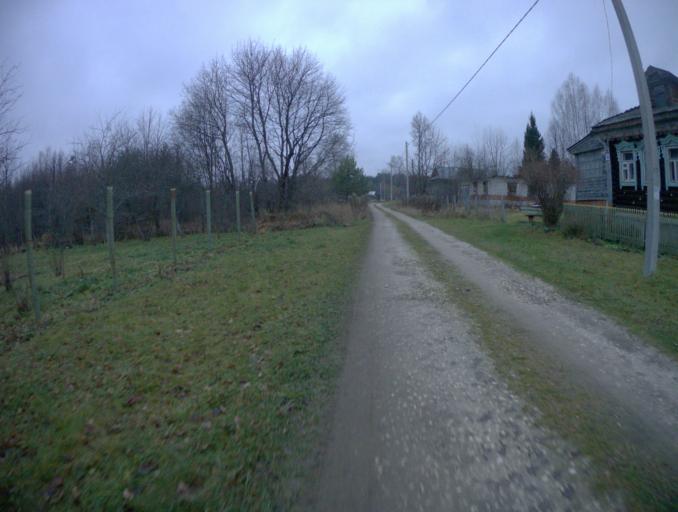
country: RU
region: Vladimir
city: Golovino
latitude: 55.9914
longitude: 40.5251
